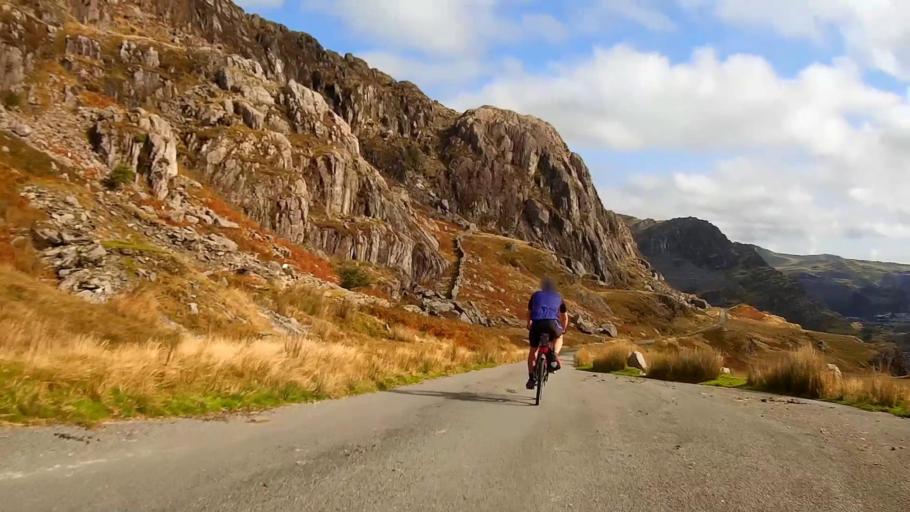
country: GB
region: Wales
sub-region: Gwynedd
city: Maentwrog
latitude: 52.9821
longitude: -3.9808
